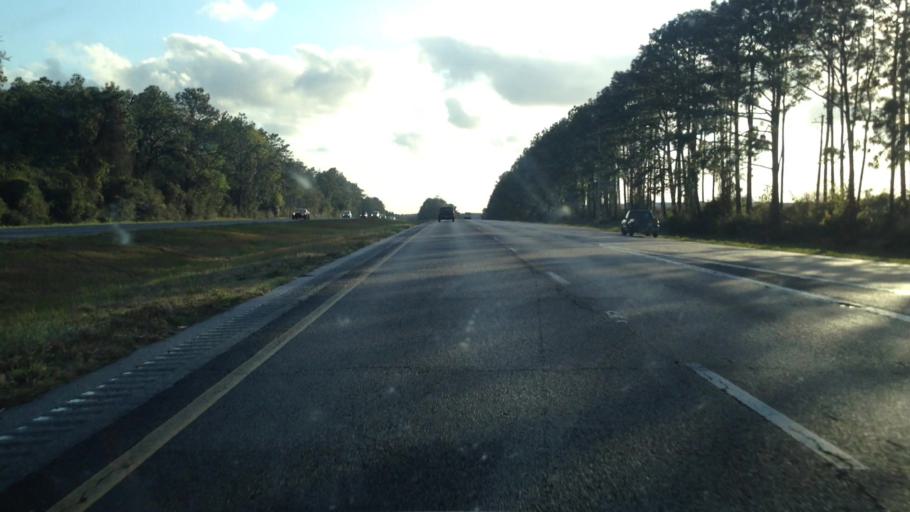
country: US
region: Alabama
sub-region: Mobile County
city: Theodore
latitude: 30.5577
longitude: -88.2053
